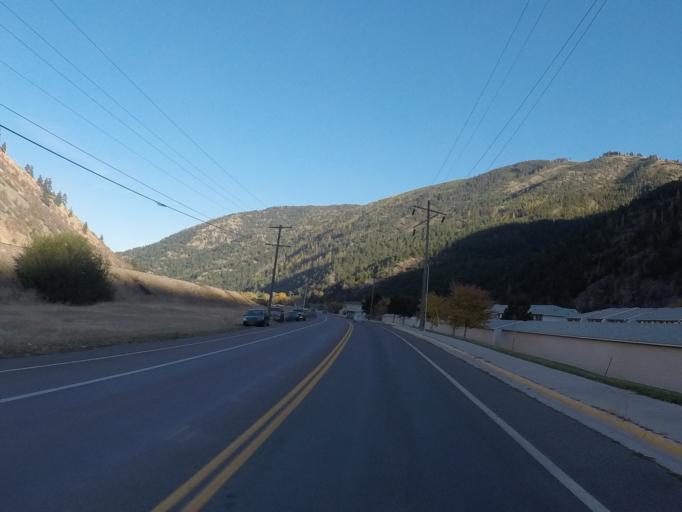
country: US
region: Montana
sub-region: Missoula County
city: East Missoula
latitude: 46.8632
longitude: -113.9687
